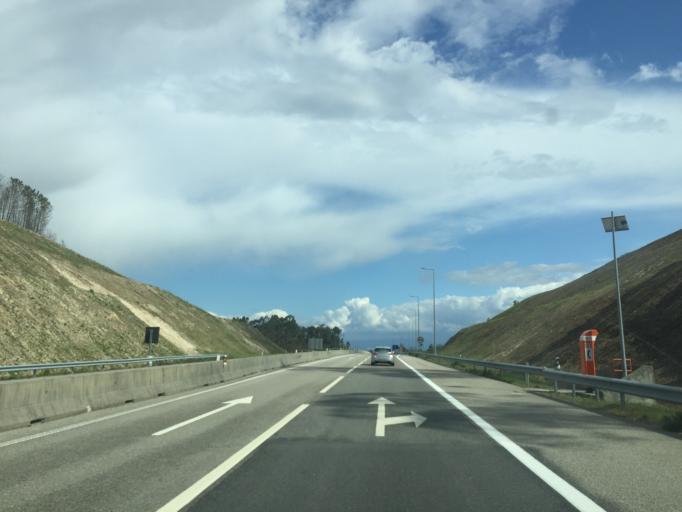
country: PT
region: Viseu
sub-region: Vouzela
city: Vouzela
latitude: 40.6520
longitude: -8.0737
